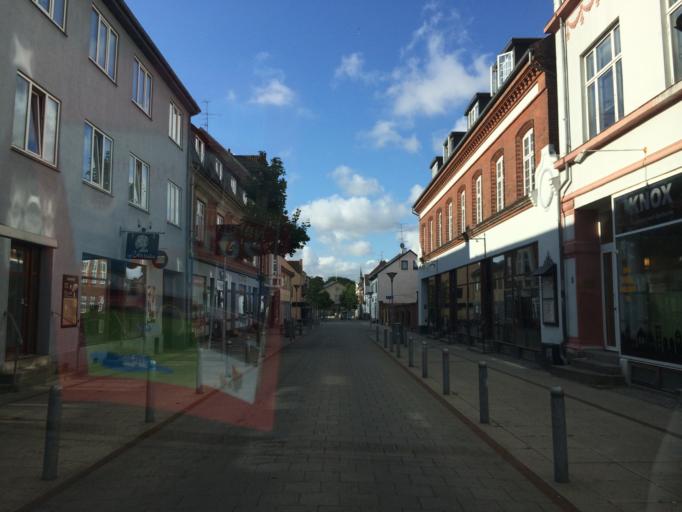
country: DK
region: North Denmark
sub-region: Hjorring Kommune
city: Hjorring
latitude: 57.4585
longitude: 9.9866
